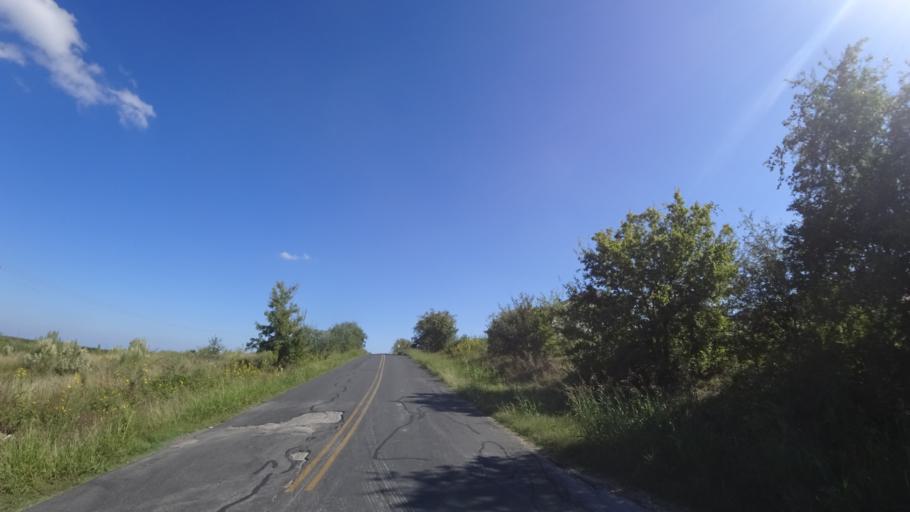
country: US
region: Texas
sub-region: Travis County
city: Manor
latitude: 30.3590
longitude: -97.6059
